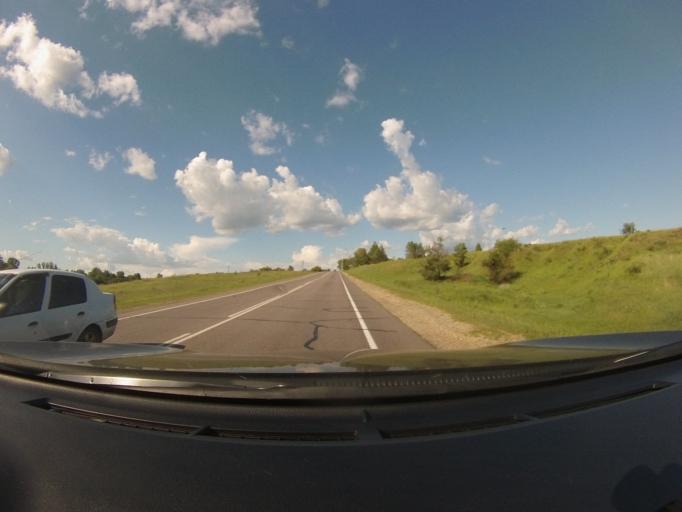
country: RU
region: Tula
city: Bol'shoye Skuratovo
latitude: 53.4242
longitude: 36.7914
